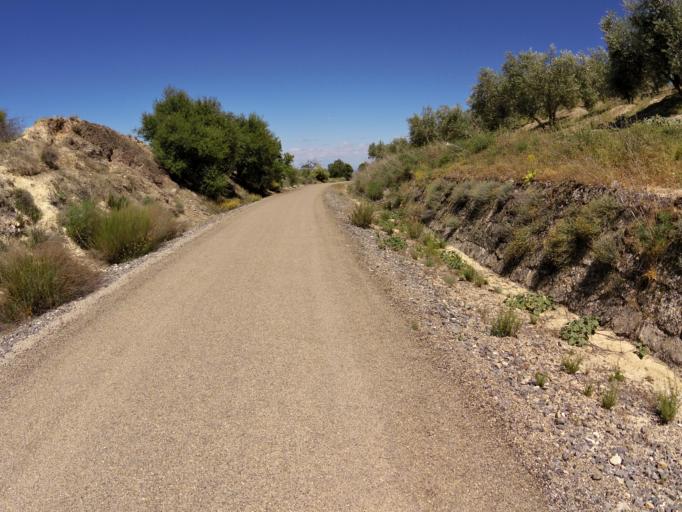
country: ES
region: Andalusia
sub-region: Provincia de Jaen
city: Torre del Campo
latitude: 37.7917
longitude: -3.8760
